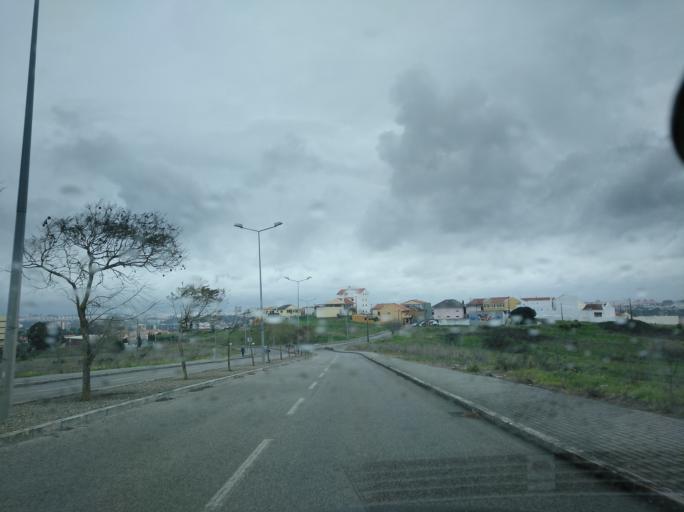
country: PT
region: Lisbon
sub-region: Odivelas
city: Famoes
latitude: 38.7902
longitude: -9.2137
